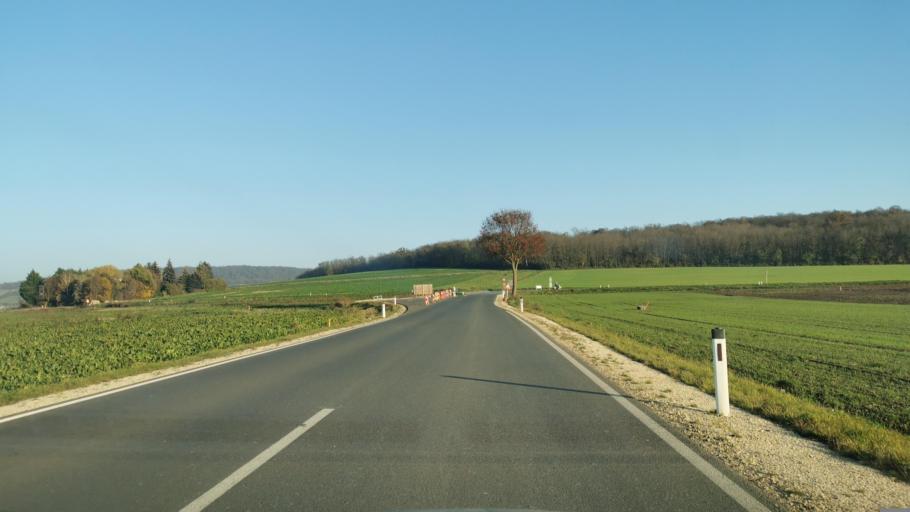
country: AT
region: Lower Austria
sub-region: Politischer Bezirk Korneuburg
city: Harmannsdorf
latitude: 48.3897
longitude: 16.3896
